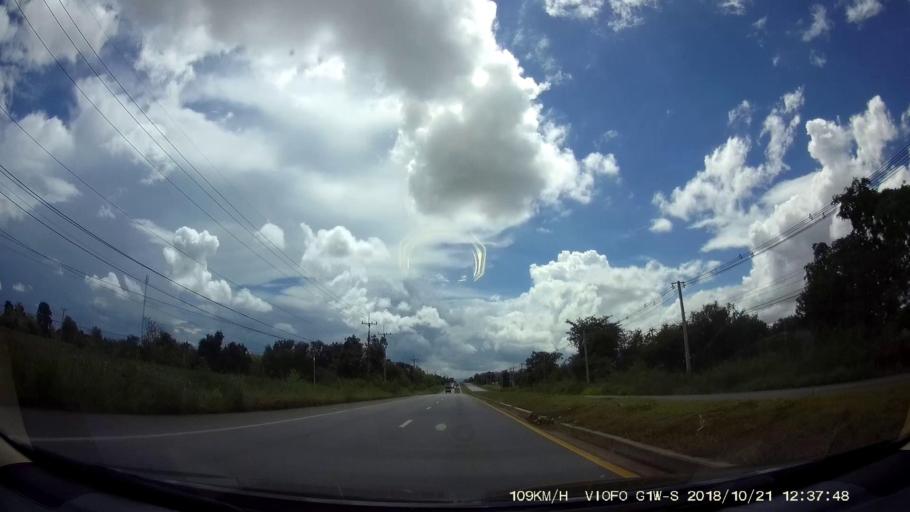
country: TH
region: Nakhon Ratchasima
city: Dan Khun Thot
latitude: 15.0635
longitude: 101.7094
